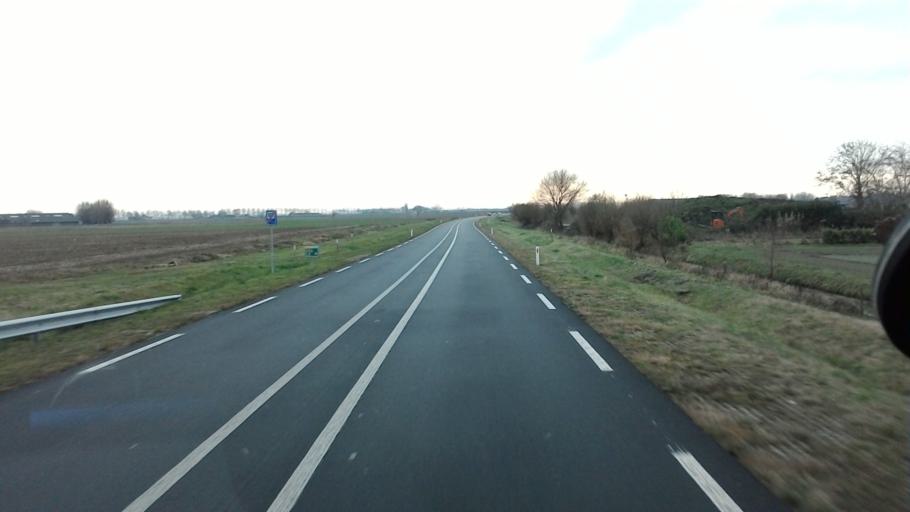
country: NL
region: Utrecht
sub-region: Gemeente Bunnik
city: Bunnik
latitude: 52.0501
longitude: 5.1948
